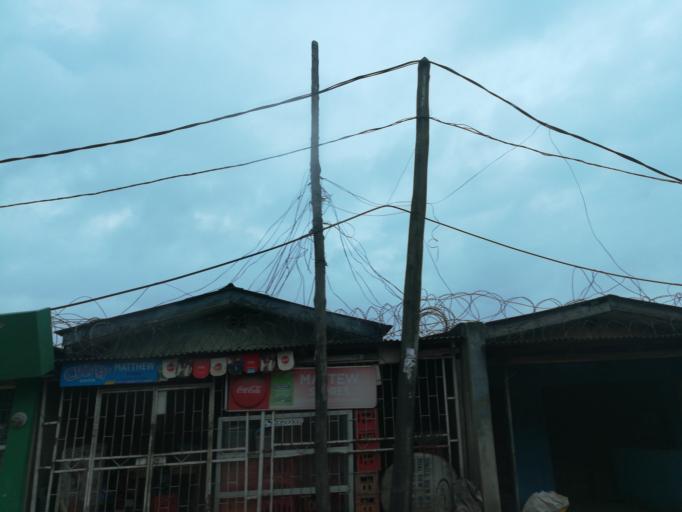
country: NG
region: Lagos
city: Oshodi
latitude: 6.5674
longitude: 3.3424
